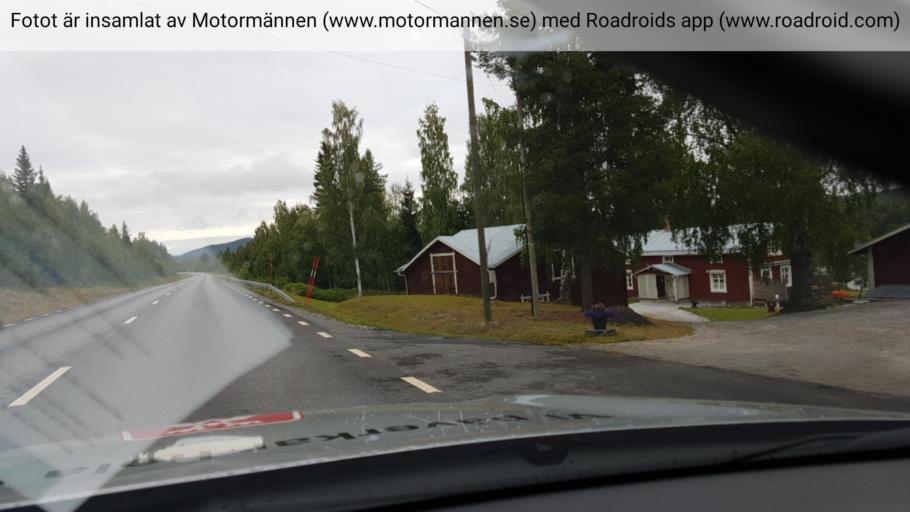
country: SE
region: Norrbotten
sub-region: Alvsbyns Kommun
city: AElvsbyn
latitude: 66.3059
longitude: 20.8008
